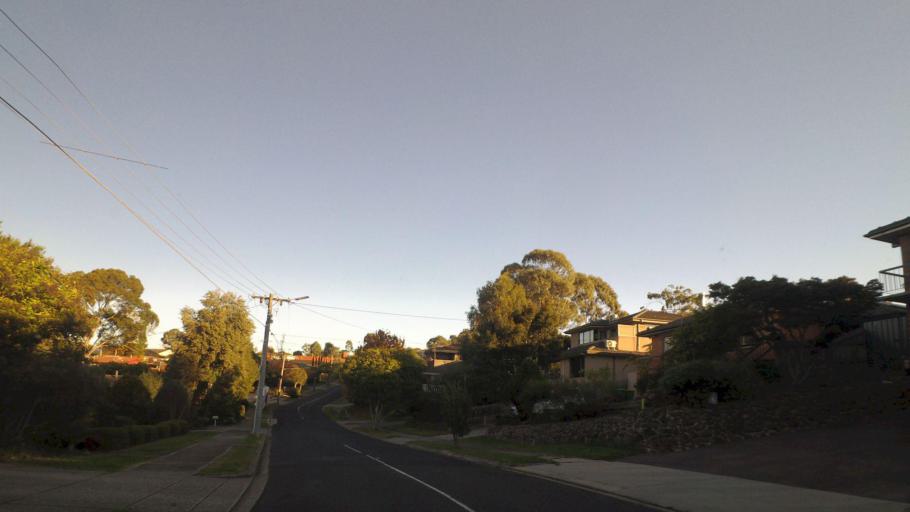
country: AU
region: Victoria
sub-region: Banyule
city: Yallambie
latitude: -37.7309
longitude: 145.0908
